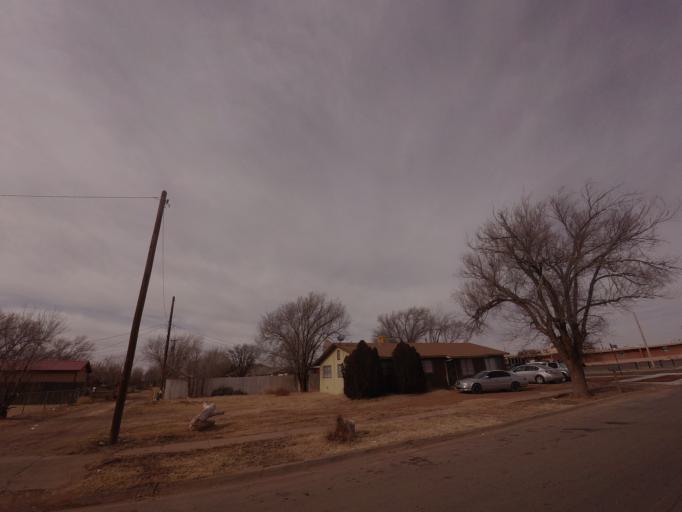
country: US
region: New Mexico
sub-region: Curry County
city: Clovis
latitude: 34.4095
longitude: -103.2404
